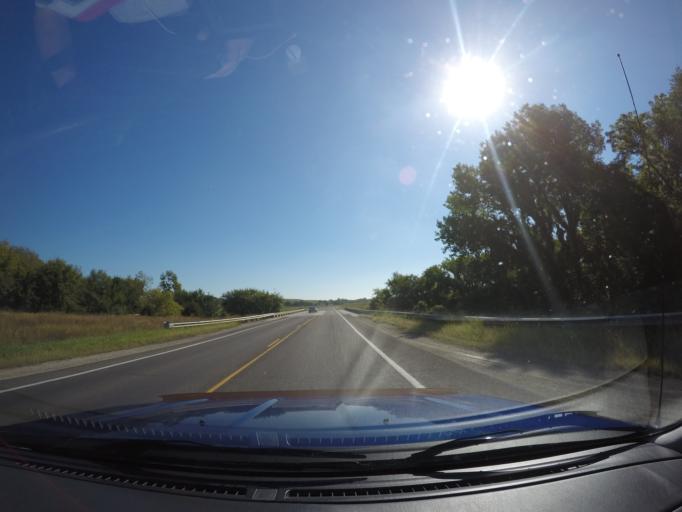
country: US
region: Kansas
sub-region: Pottawatomie County
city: Saint Marys
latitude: 39.2168
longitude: -96.1270
